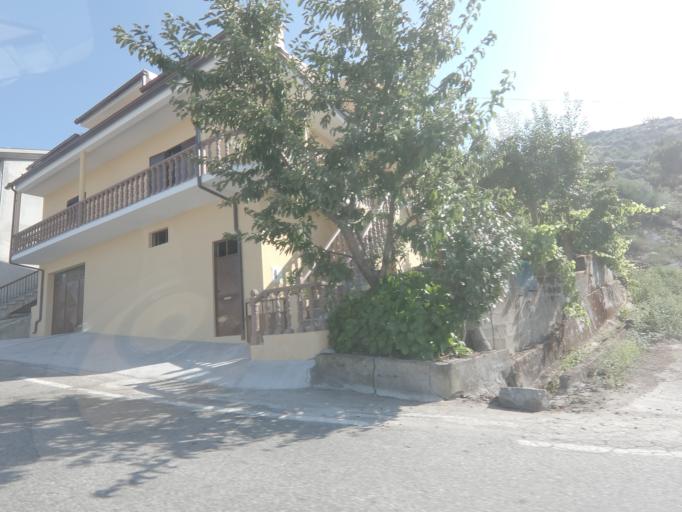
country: PT
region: Viseu
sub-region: Tabuaco
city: Tabuaco
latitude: 41.1147
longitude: -7.5702
